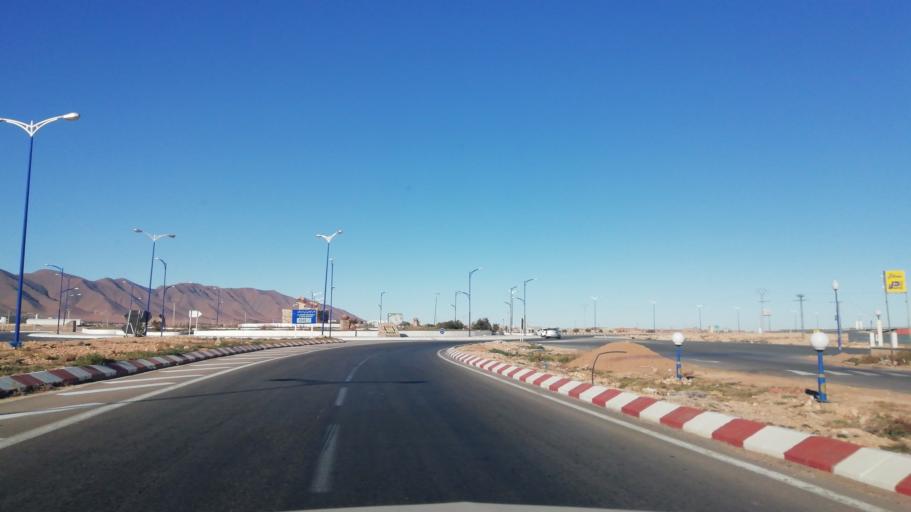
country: DZ
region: Wilaya de Naama
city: Naama
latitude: 33.5099
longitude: -0.2868
